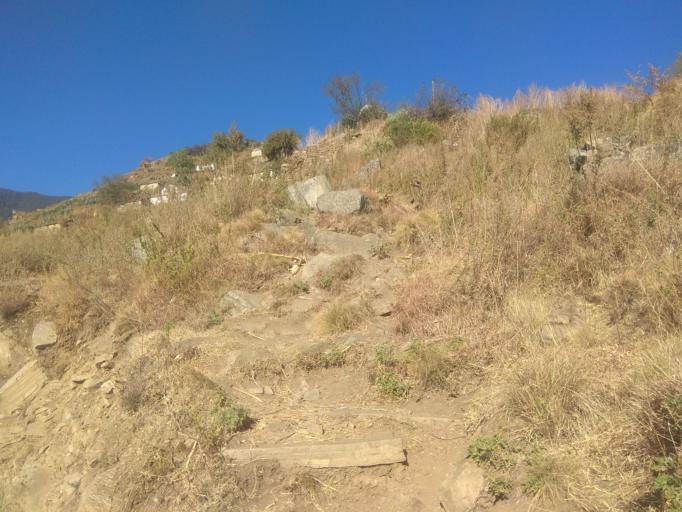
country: NP
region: Mid Western
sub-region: Bheri Zone
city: Dailekh
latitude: 29.2880
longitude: 81.7110
